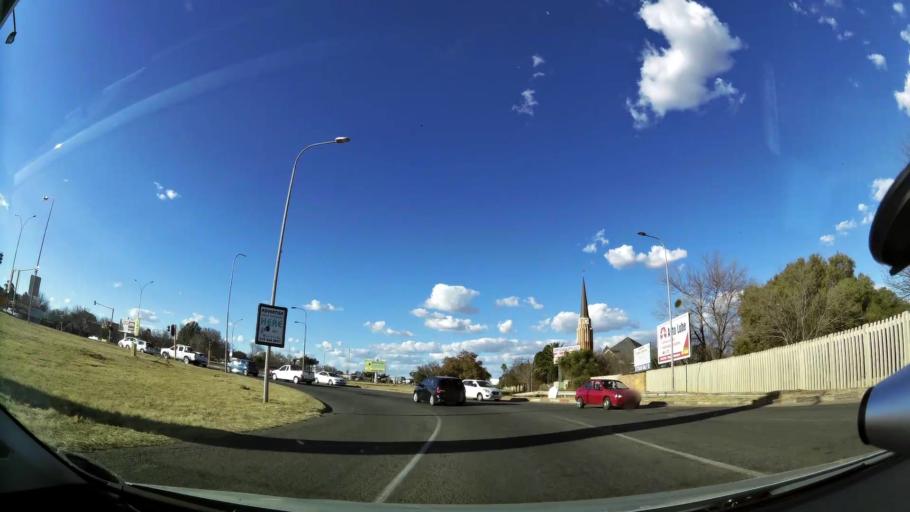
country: ZA
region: North-West
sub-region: Dr Kenneth Kaunda District Municipality
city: Klerksdorp
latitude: -26.8589
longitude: 26.6720
